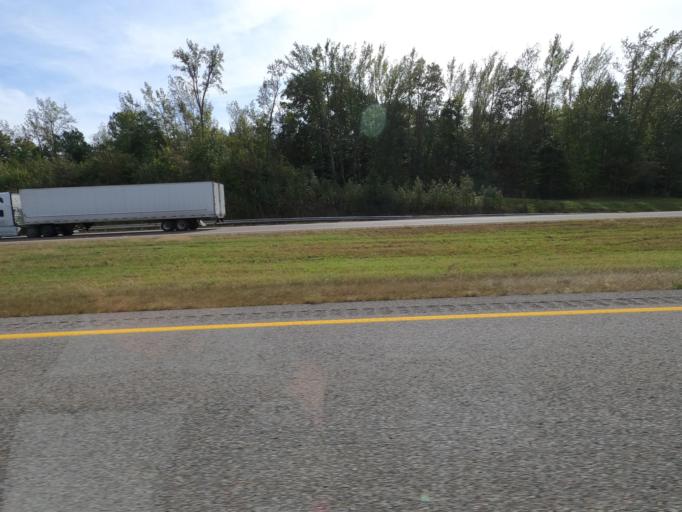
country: US
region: Tennessee
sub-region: Humphreys County
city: New Johnsonville
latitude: 35.8519
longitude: -88.0651
